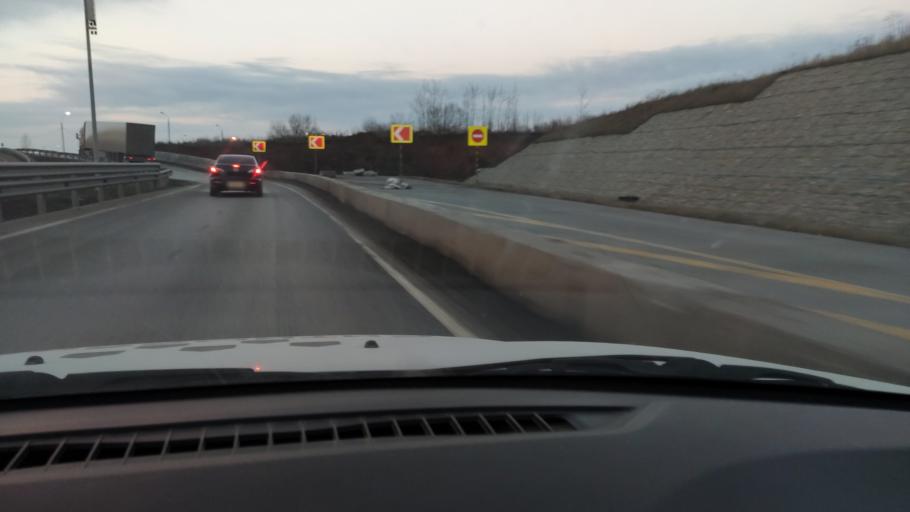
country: RU
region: Perm
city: Lobanovo
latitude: 57.8305
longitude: 56.2996
